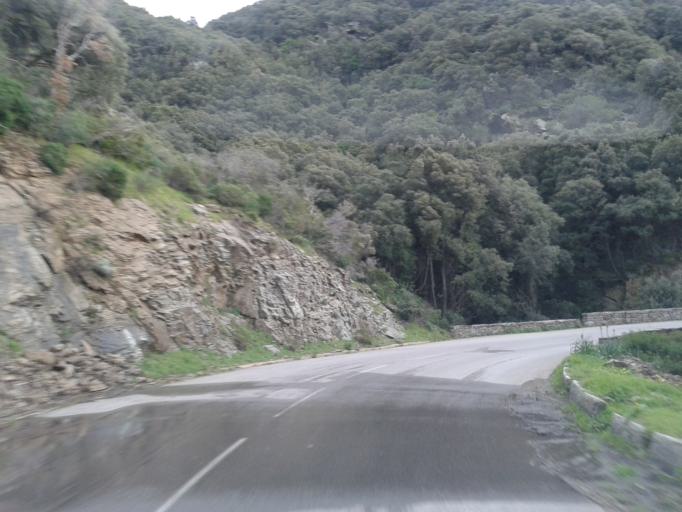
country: FR
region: Corsica
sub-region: Departement de la Haute-Corse
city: Brando
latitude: 42.8837
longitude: 9.3346
